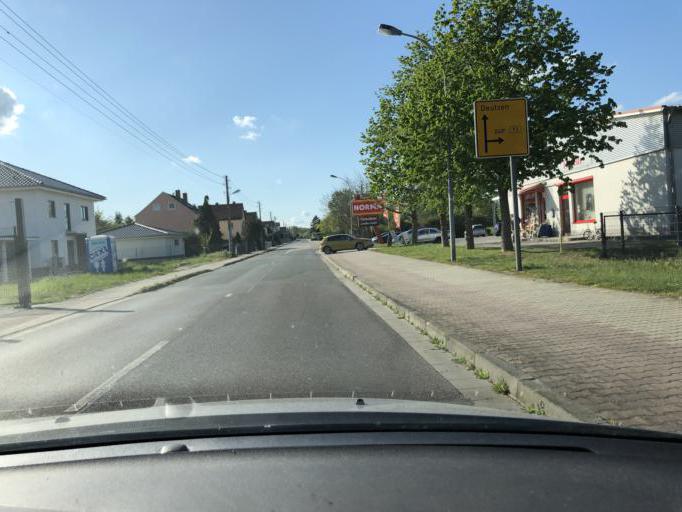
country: DE
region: Saxony
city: Regis-Breitingen
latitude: 51.0932
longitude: 12.4439
